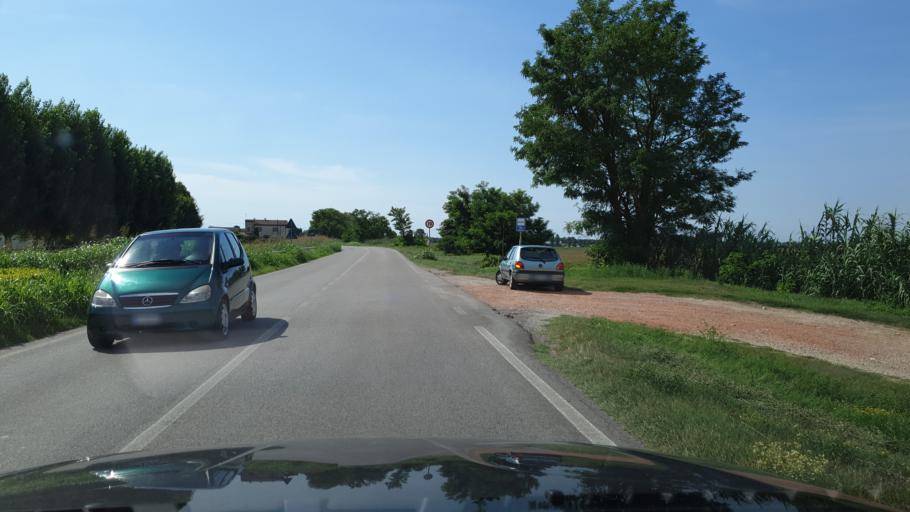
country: IT
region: Veneto
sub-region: Provincia di Rovigo
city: Fratta Polesine
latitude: 45.0189
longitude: 11.6390
